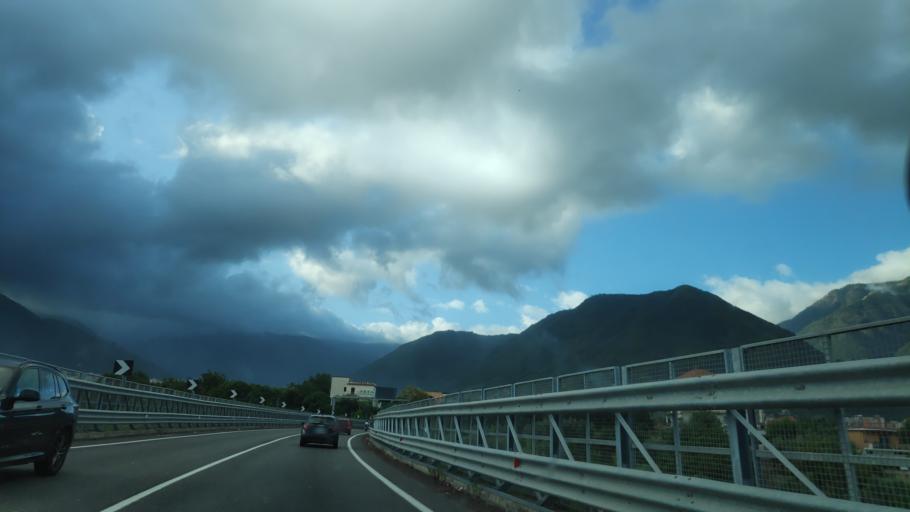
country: IT
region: Campania
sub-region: Provincia di Napoli
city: Santa Maria La Carita
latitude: 40.7046
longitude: 14.5027
